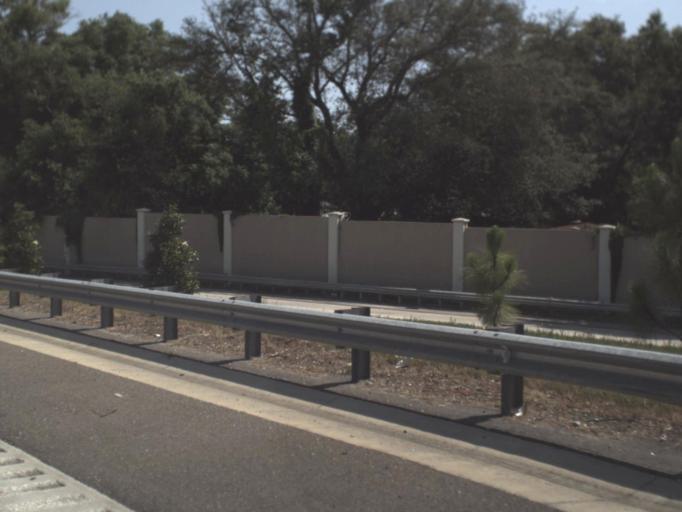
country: US
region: Florida
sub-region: Duval County
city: Jacksonville
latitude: 30.3933
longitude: -81.6678
